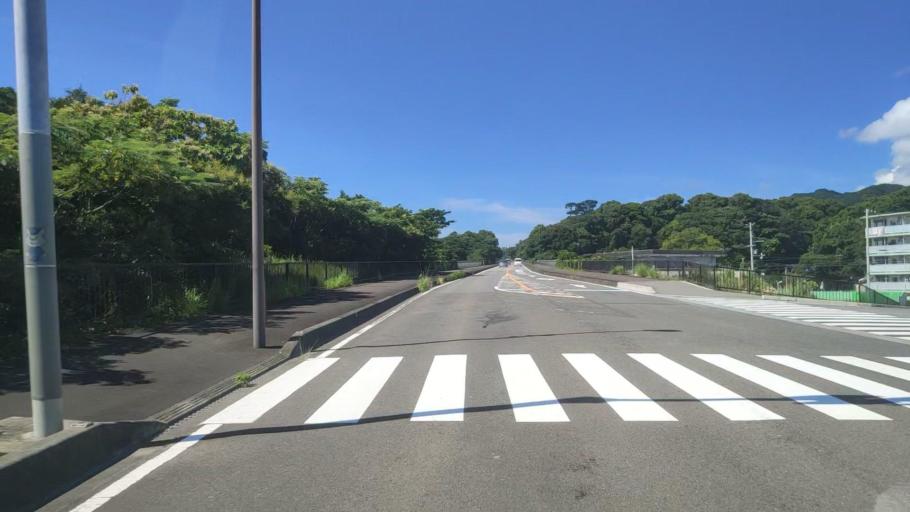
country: JP
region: Wakayama
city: Shingu
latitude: 33.7115
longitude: 135.9985
